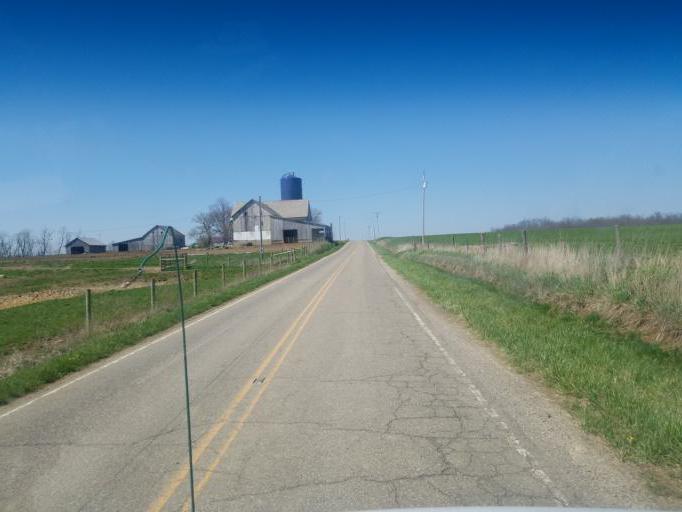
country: US
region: Ohio
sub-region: Knox County
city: Oak Hill
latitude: 40.3223
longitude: -82.1794
